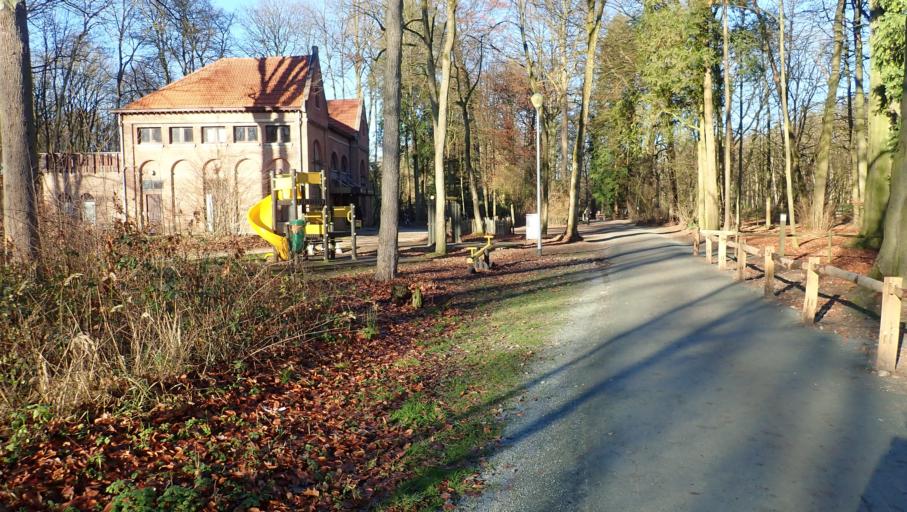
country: BE
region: Flanders
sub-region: Provincie Antwerpen
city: Schilde
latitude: 51.2484
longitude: 4.6284
